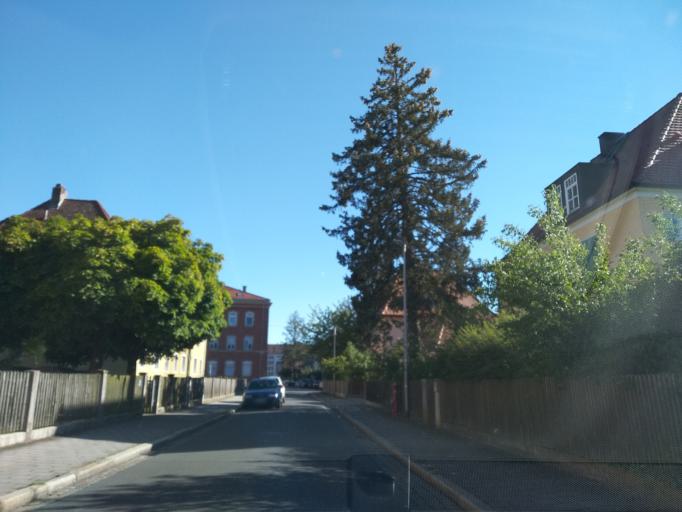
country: DE
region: Bavaria
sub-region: Regierungsbezirk Mittelfranken
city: Erlangen
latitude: 49.5989
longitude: 11.0245
